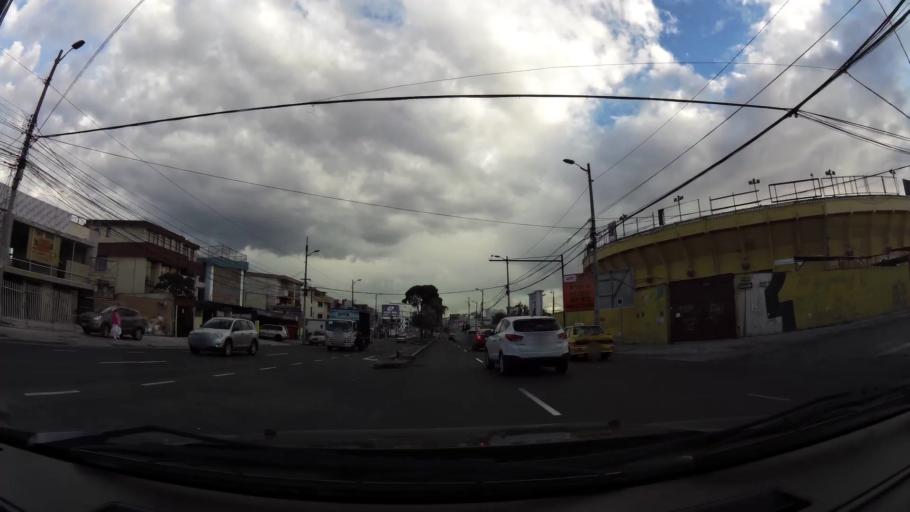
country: EC
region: Pichincha
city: Quito
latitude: -0.1627
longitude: -78.4833
